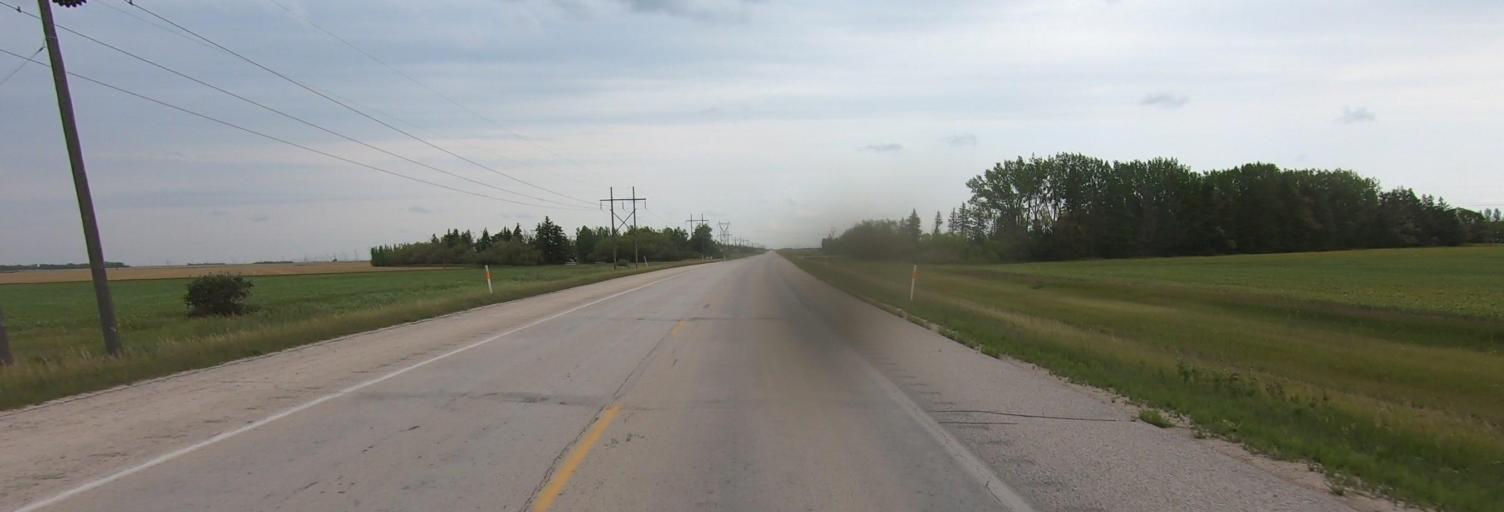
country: CA
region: Manitoba
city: Headingley
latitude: 49.7370
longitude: -97.3606
